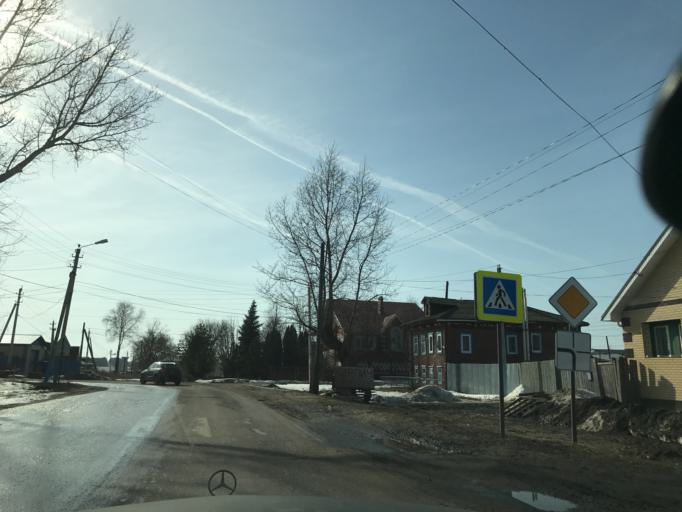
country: RU
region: Nizjnij Novgorod
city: Taremskoye
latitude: 55.9561
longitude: 43.0451
